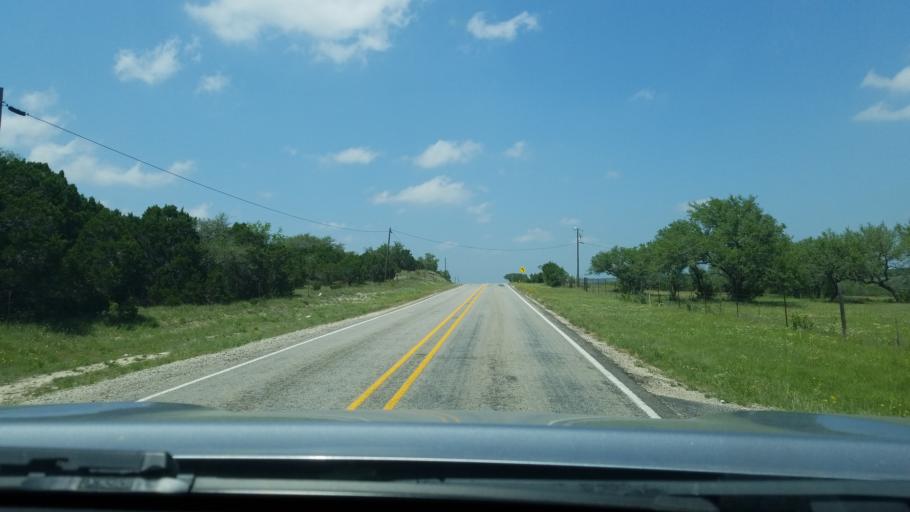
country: US
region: Texas
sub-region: Hays County
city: Woodcreek
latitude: 30.0735
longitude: -98.2209
